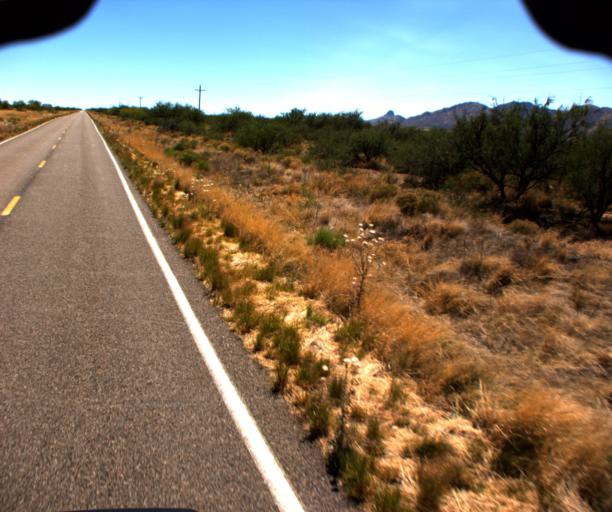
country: US
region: Arizona
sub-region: Pima County
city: Three Points
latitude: 31.7833
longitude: -111.4591
